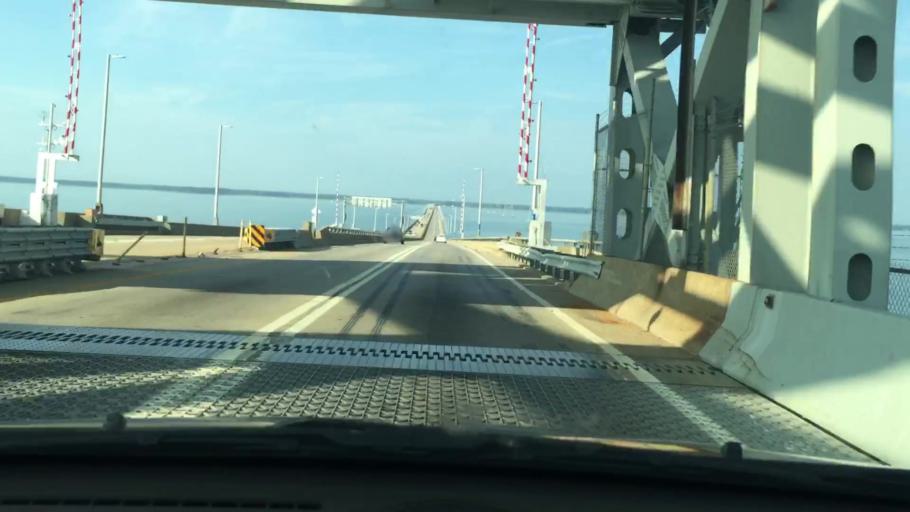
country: US
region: Virginia
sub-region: City of Newport News
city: Newport News
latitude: 37.0025
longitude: -76.4693
